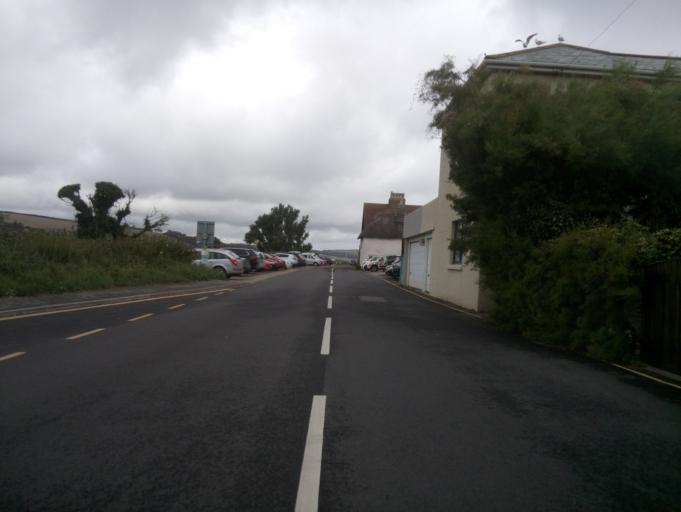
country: GB
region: England
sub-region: Devon
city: Dartmouth
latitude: 50.2668
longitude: -3.6529
